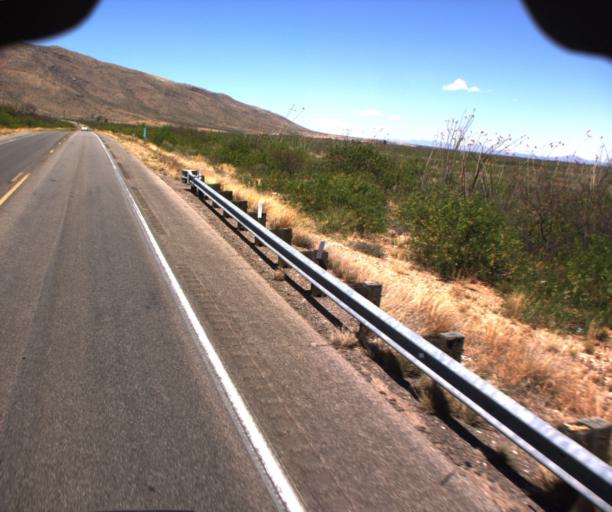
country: US
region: Arizona
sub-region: Cochise County
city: Bisbee
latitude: 31.4333
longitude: -109.8133
